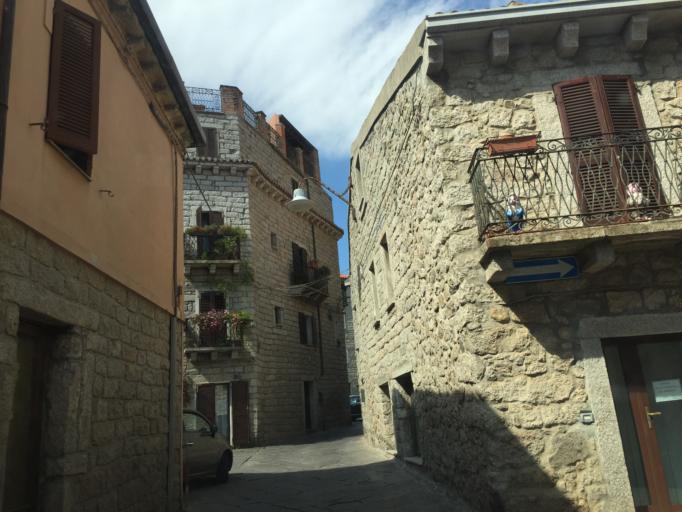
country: IT
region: Sardinia
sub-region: Provincia di Olbia-Tempio
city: Tempio Pausania
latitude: 40.9035
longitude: 9.1038
